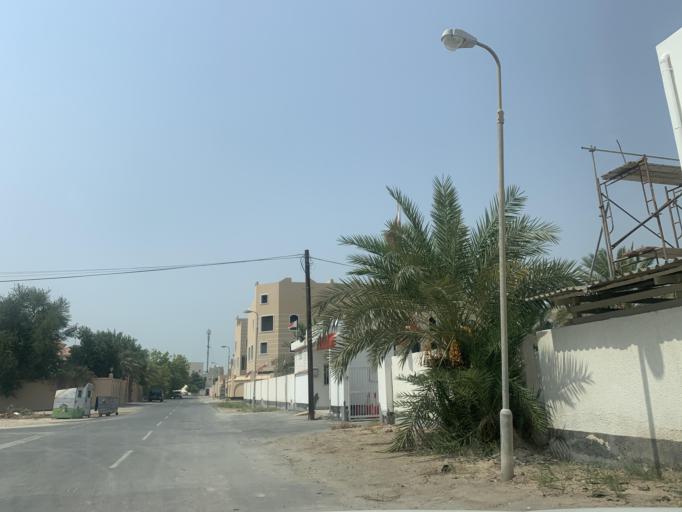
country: BH
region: Central Governorate
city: Madinat Hamad
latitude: 26.1624
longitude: 50.4540
